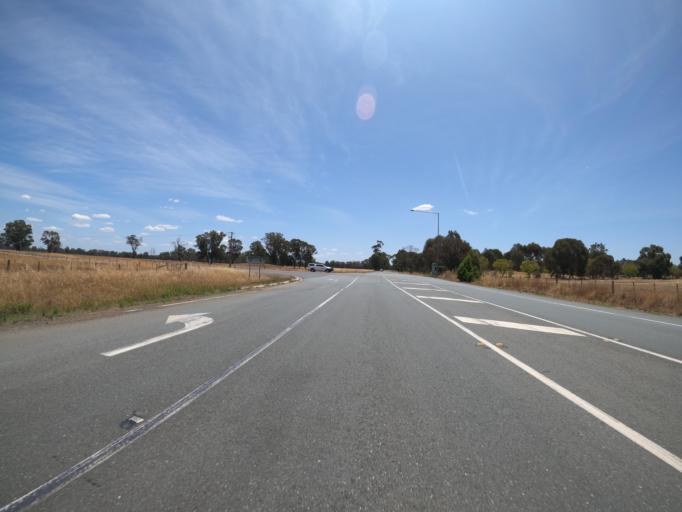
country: AU
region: Victoria
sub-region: Benalla
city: Benalla
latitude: -36.4981
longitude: 146.0203
